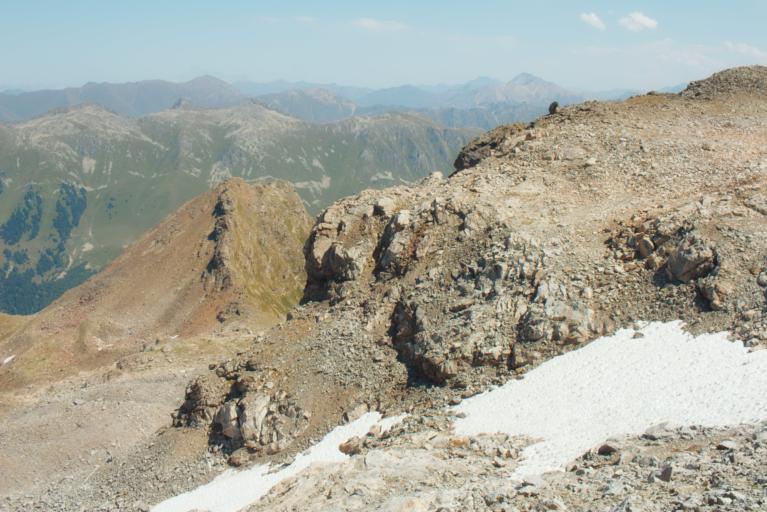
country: RU
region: Karachayevo-Cherkesiya
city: Nizhniy Arkhyz
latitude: 43.4547
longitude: 41.2188
